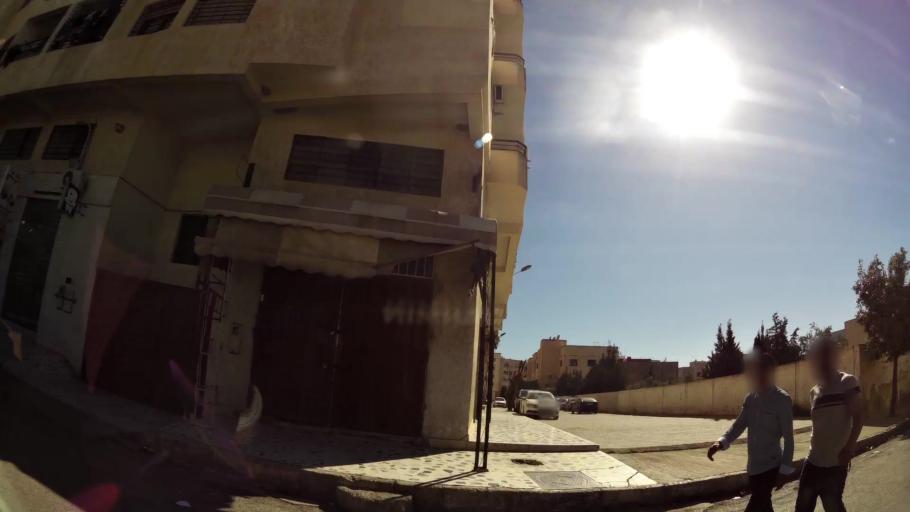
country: MA
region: Fes-Boulemane
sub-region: Fes
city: Fes
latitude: 34.0172
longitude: -4.9743
